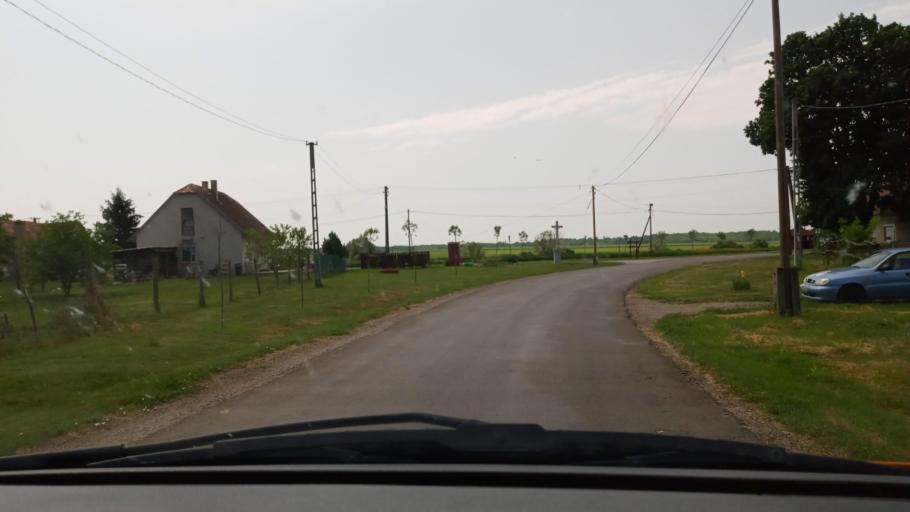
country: HU
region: Baranya
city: Szentlorinc
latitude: 45.9928
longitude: 18.0343
